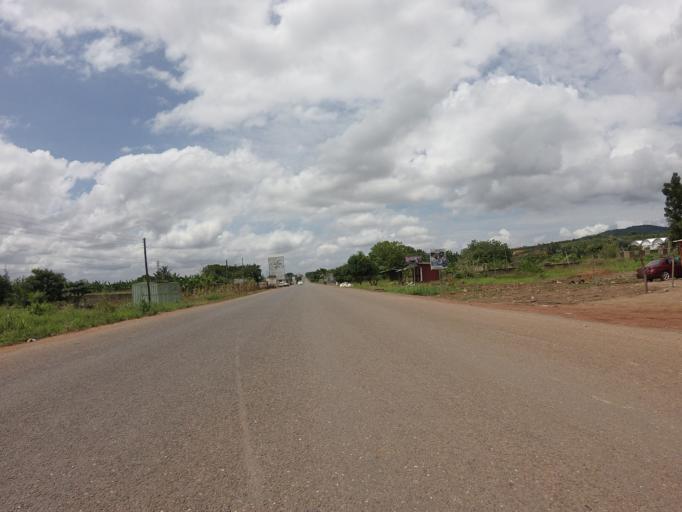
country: GH
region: Eastern
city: Aburi
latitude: 5.8345
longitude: -0.1172
